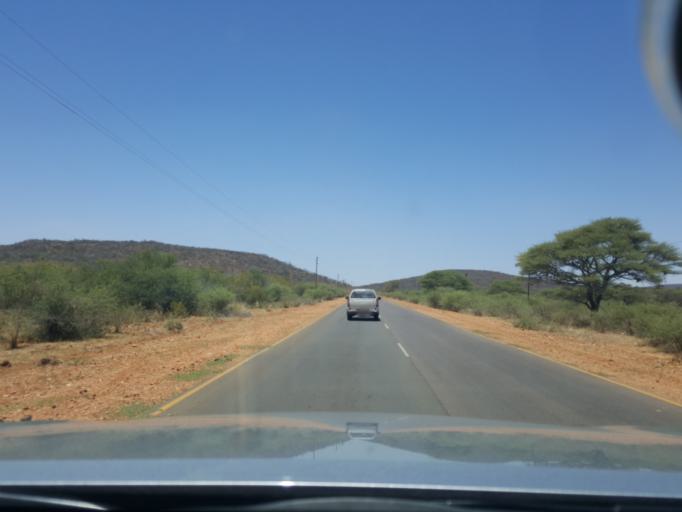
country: ZA
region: North-West
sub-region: Ngaka Modiri Molema District Municipality
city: Zeerust
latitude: -25.3736
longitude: 25.9353
